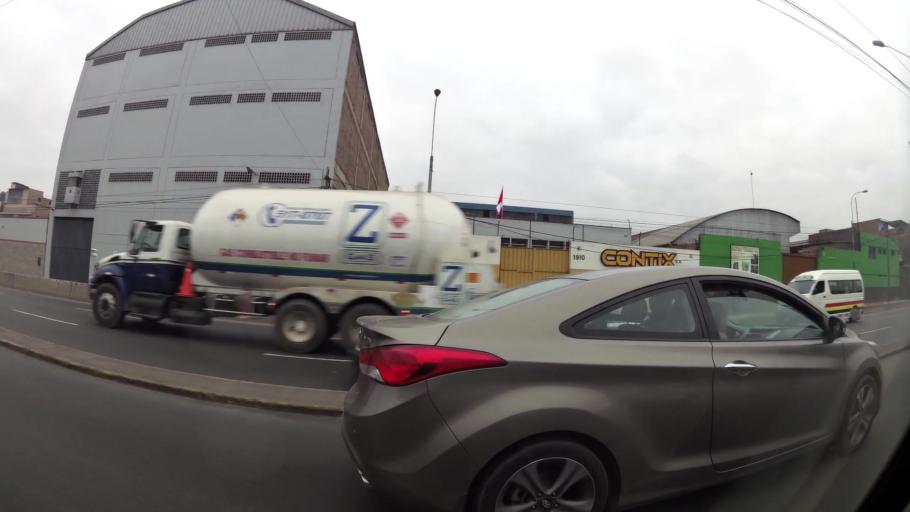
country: PE
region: Lima
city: Lima
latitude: -12.0487
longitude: -77.0658
